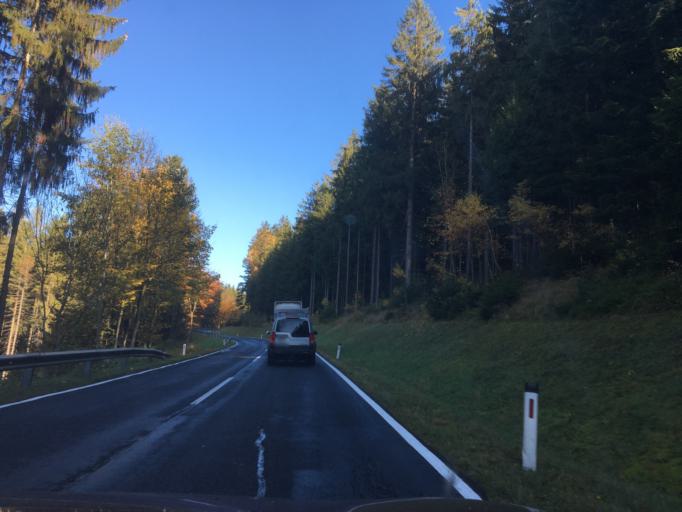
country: AT
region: Upper Austria
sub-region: Politischer Bezirk Freistadt
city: Freistadt
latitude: 48.5010
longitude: 14.6139
